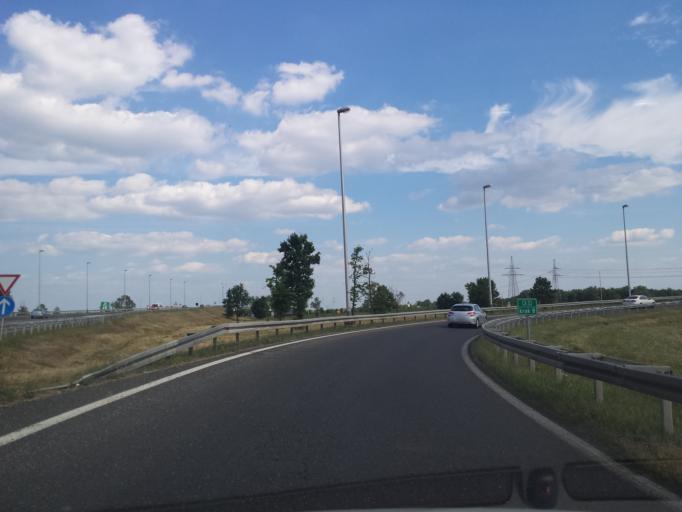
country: HR
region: Grad Zagreb
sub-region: Sesvete
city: Sesvete
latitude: 45.7996
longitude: 16.1329
